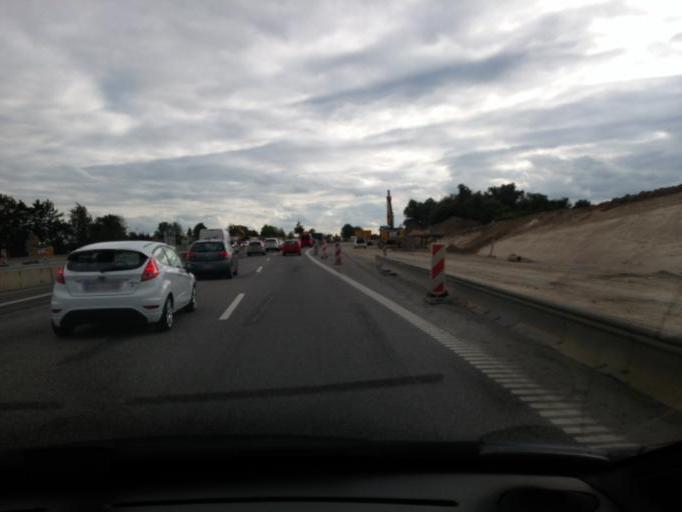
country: DK
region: Zealand
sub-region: Koge Kommune
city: Koge
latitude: 55.4848
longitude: 12.1624
